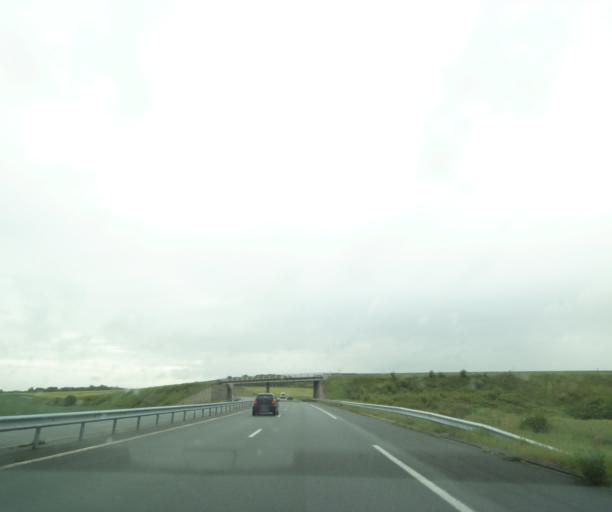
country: FR
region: Poitou-Charentes
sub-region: Departement de la Charente-Maritime
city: Nieul-les-Saintes
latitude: 45.6974
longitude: -0.7410
